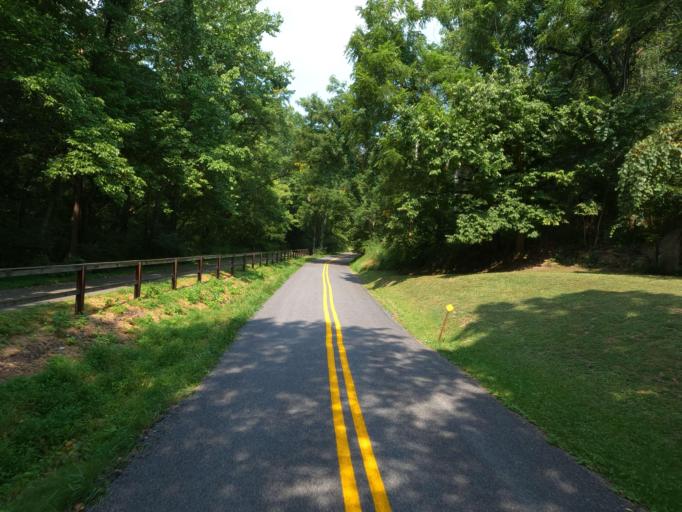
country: US
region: West Virginia
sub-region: Morgan County
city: Berkeley Springs
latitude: 39.6339
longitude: -78.3153
